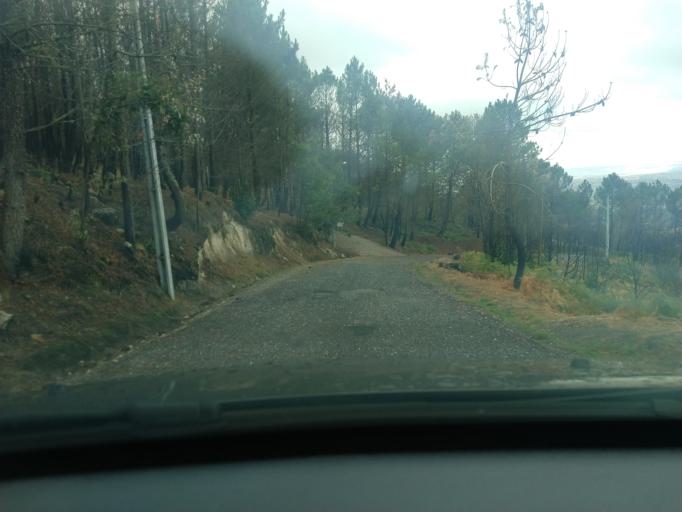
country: PT
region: Guarda
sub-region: Seia
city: Seia
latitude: 40.4192
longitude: -7.6707
